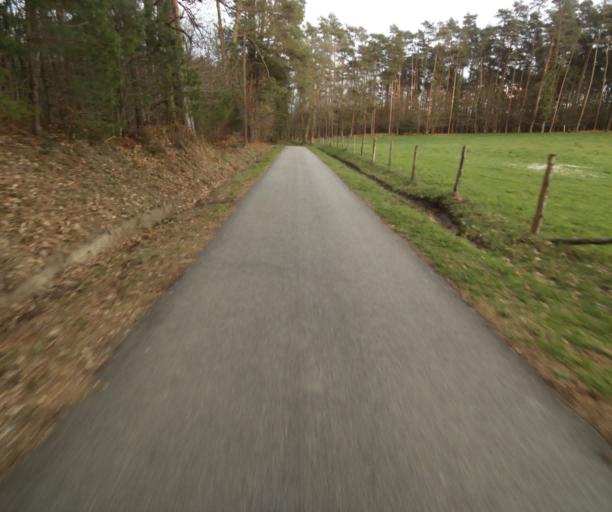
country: FR
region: Limousin
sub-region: Departement de la Correze
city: Argentat
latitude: 45.2238
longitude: 1.9499
